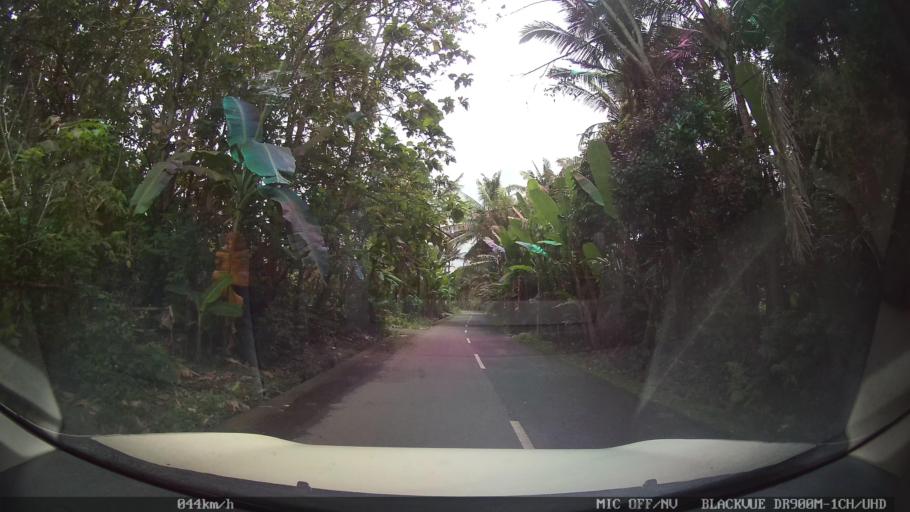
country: ID
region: Bali
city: Banjar Parekan
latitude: -8.5805
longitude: 115.2120
